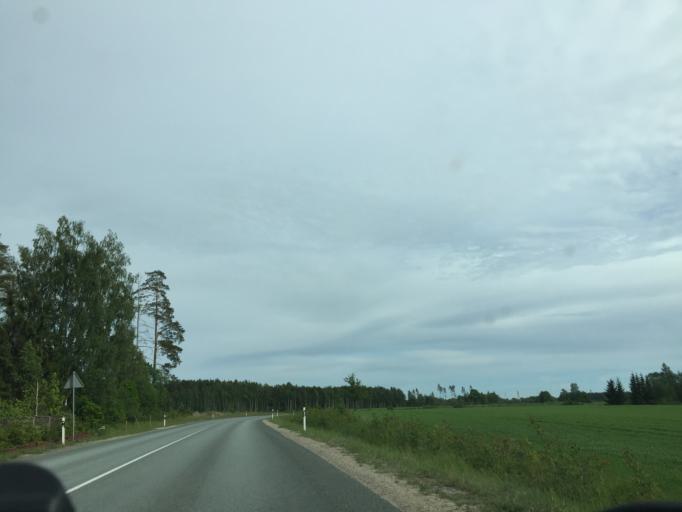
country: LV
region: Beverina
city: Murmuiza
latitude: 57.4666
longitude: 25.4123
